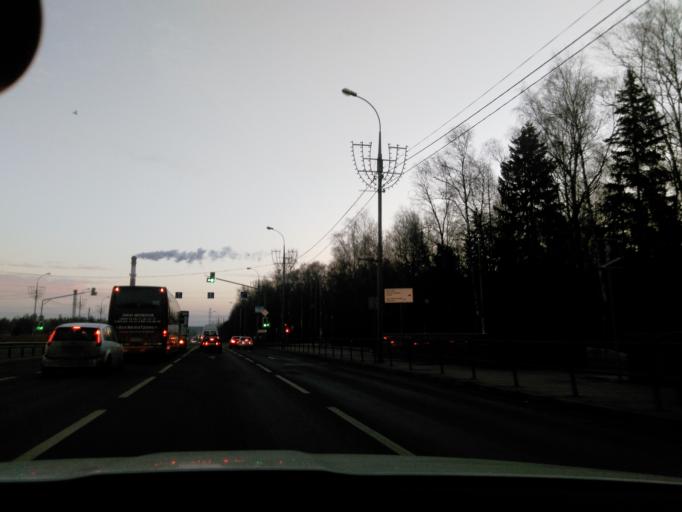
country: RU
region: Moscow
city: Zelenograd
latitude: 55.9988
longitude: 37.1930
